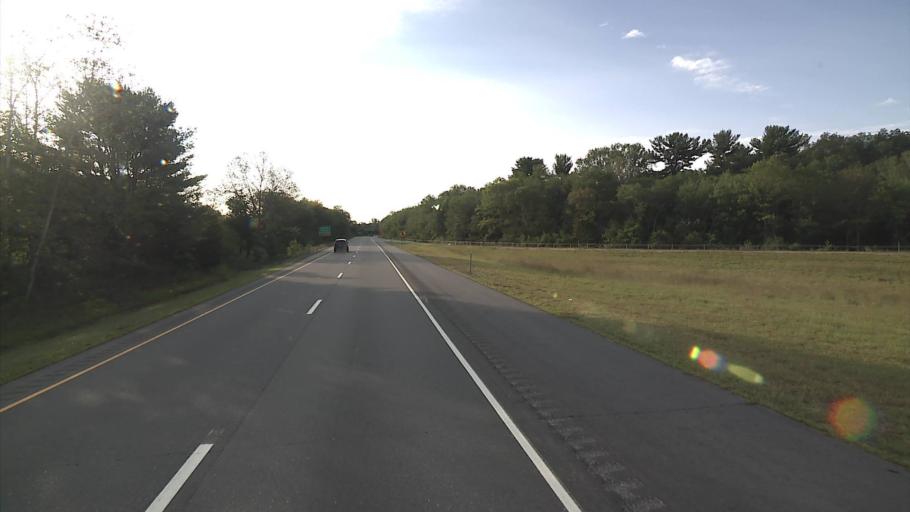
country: US
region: Connecticut
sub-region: New London County
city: Colchester
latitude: 41.5689
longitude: -72.3362
